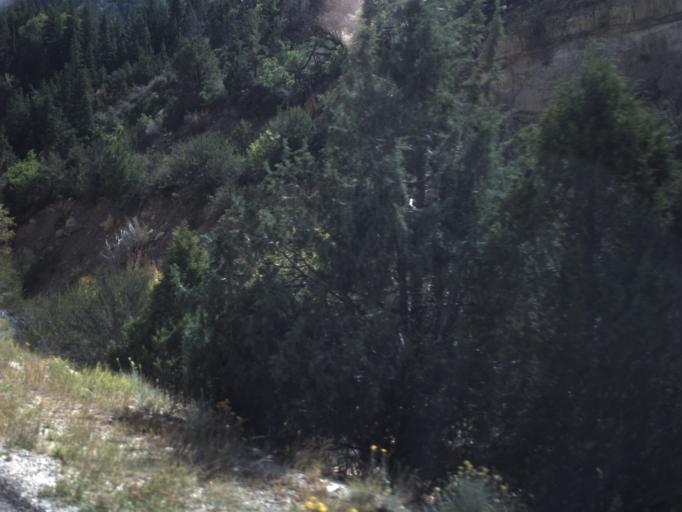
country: US
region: Utah
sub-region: Iron County
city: Cedar City
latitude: 37.6423
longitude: -112.9567
